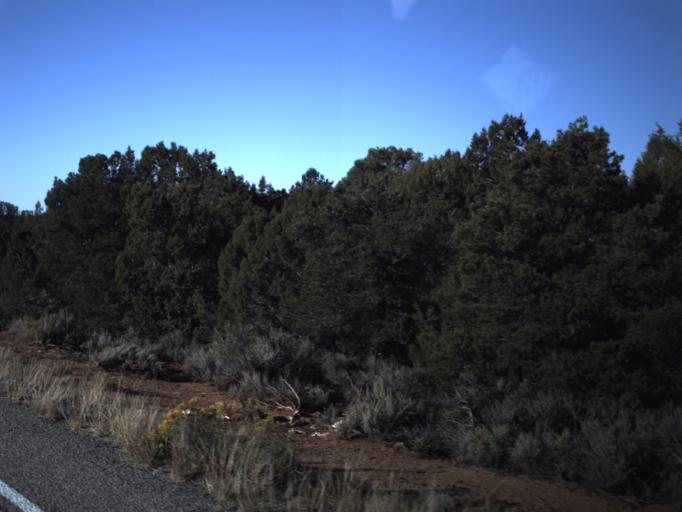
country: US
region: Utah
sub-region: San Juan County
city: Blanding
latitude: 37.5610
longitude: -109.9308
